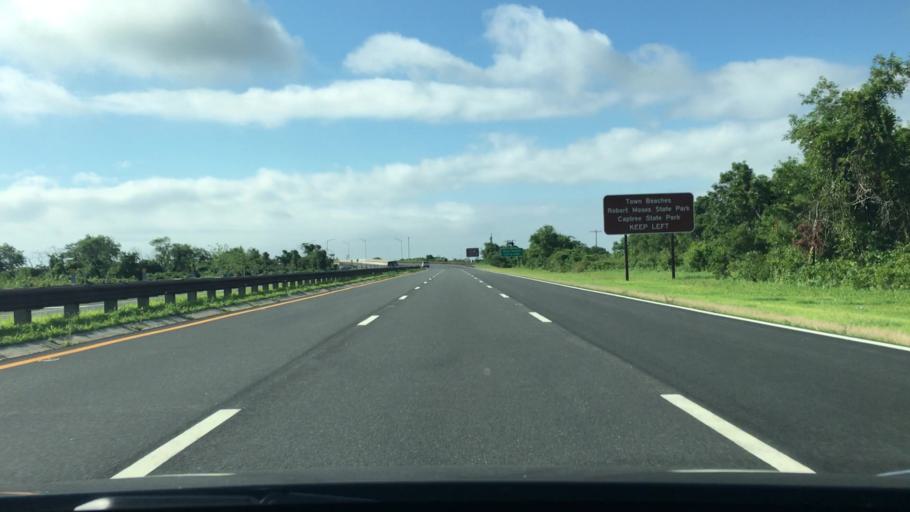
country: US
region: New York
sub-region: Nassau County
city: Seaford
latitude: 40.6274
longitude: -73.5027
